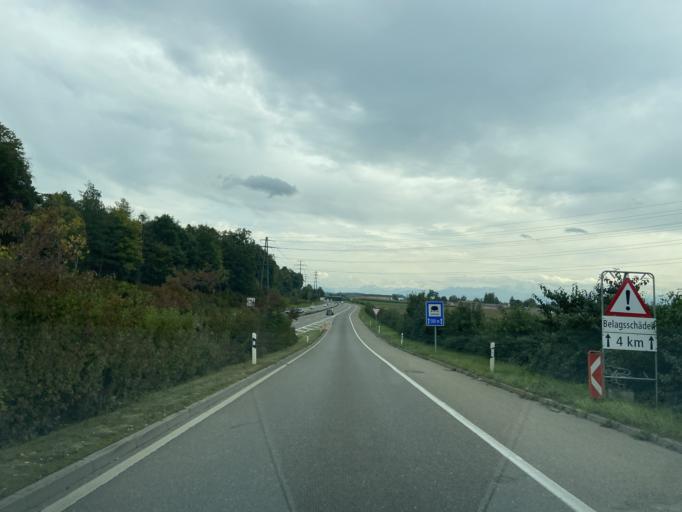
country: CH
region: Zurich
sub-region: Bezirk Uster
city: Greifensee / Muellerwis / Seilerwis
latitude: 47.3805
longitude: 8.6857
